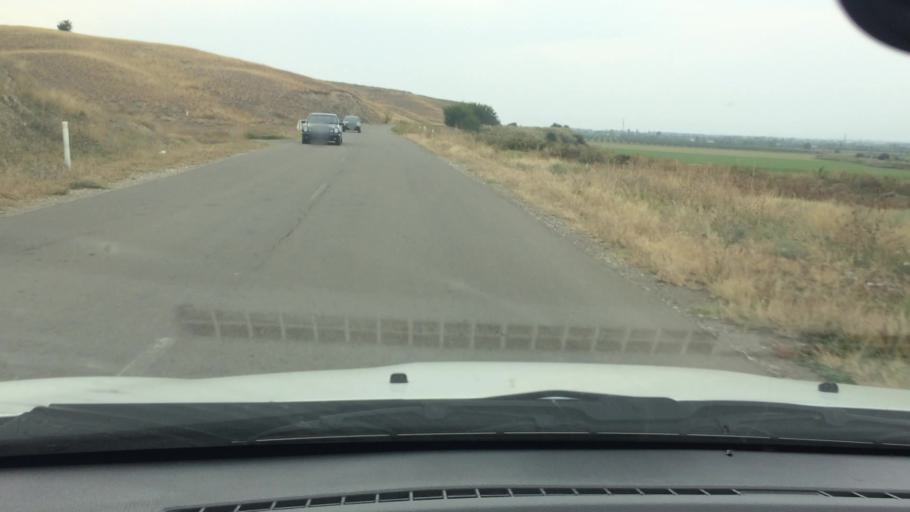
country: AM
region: Tavush
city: Berdavan
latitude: 41.3393
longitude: 44.9993
